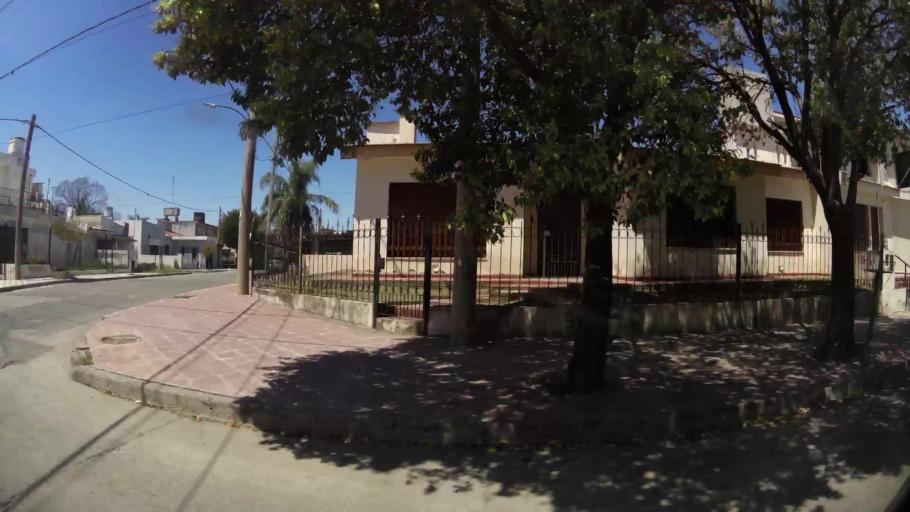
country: AR
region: Cordoba
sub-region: Departamento de Capital
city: Cordoba
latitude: -31.3895
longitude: -64.1400
